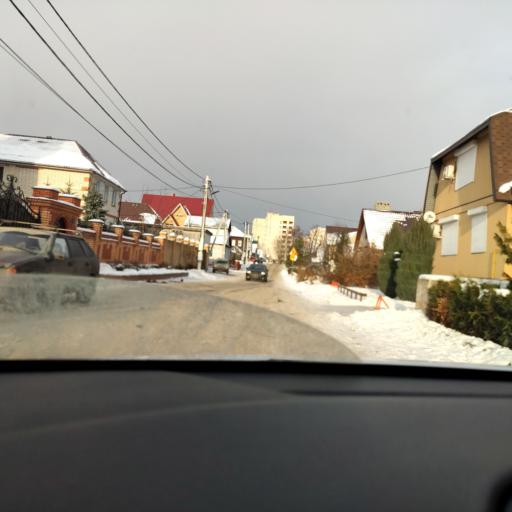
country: RU
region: Tatarstan
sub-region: Gorod Kazan'
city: Kazan
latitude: 55.7937
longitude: 49.0594
